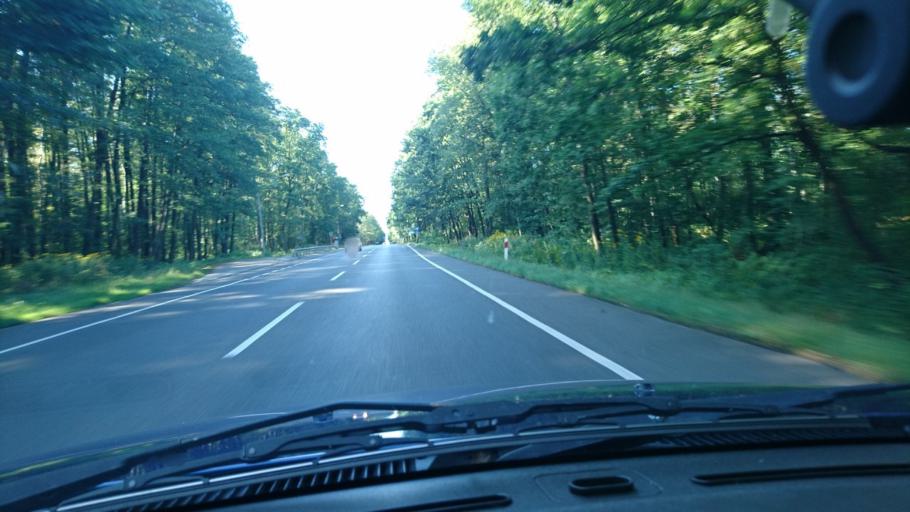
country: PL
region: Silesian Voivodeship
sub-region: Gliwice
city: Gliwice
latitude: 50.3361
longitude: 18.6552
